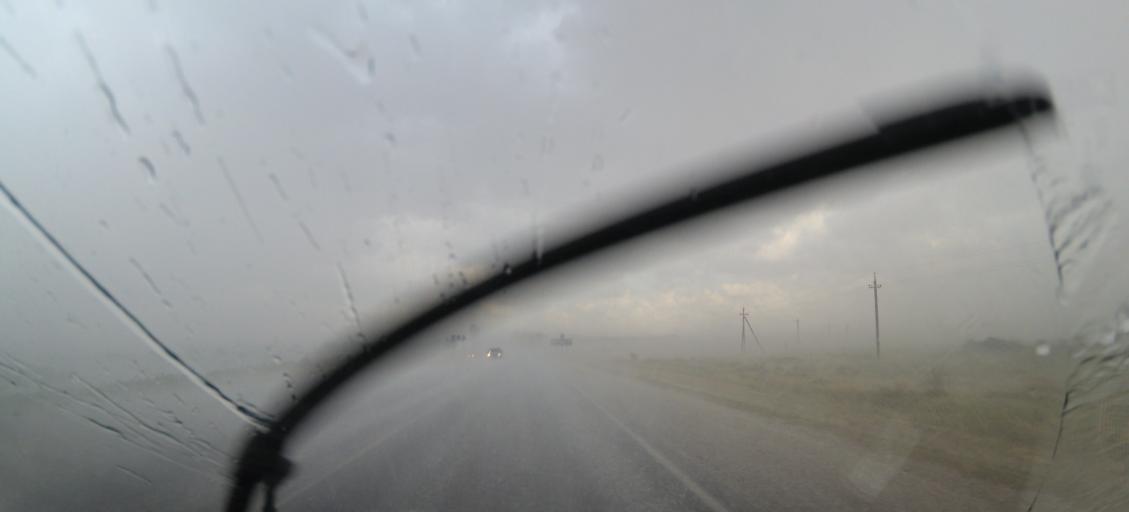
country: RU
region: Rostov
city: Proletarsk
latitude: 46.6914
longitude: 41.7389
